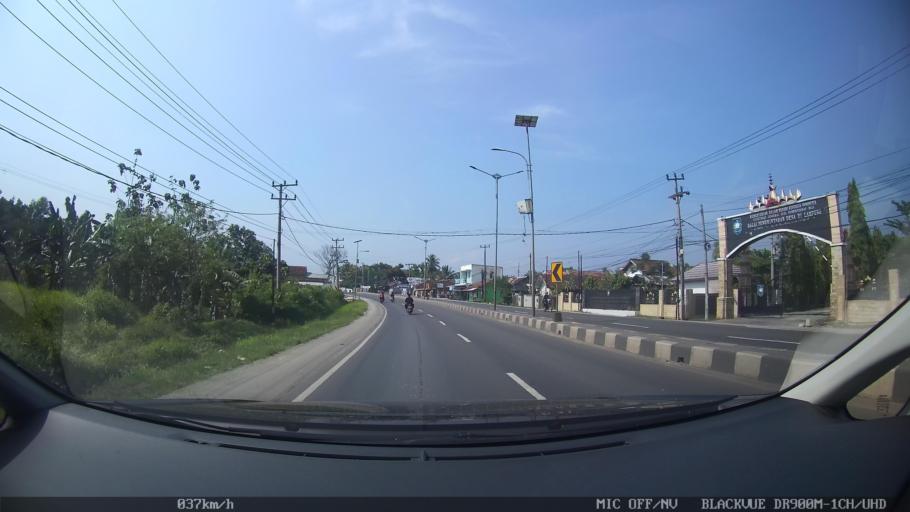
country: ID
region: Lampung
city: Natar
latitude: -5.2609
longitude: 105.1846
